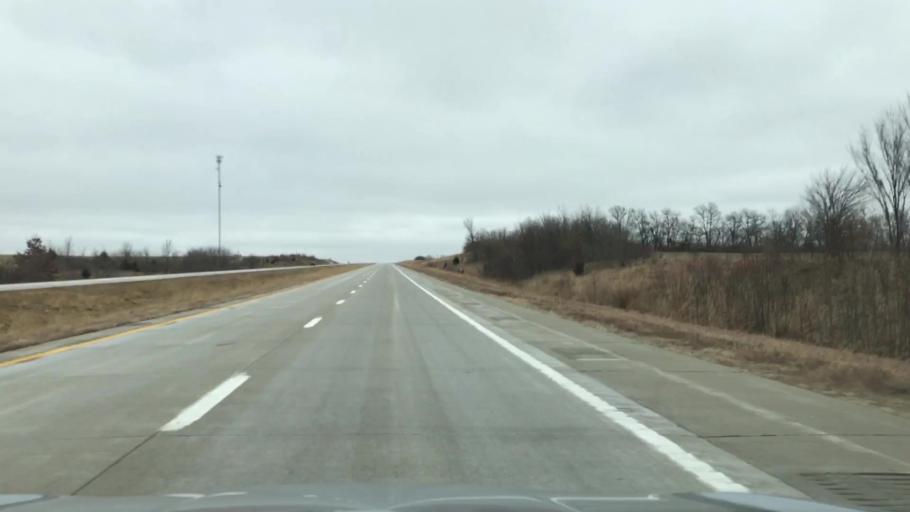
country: US
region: Missouri
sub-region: Caldwell County
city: Hamilton
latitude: 39.7348
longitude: -93.7764
